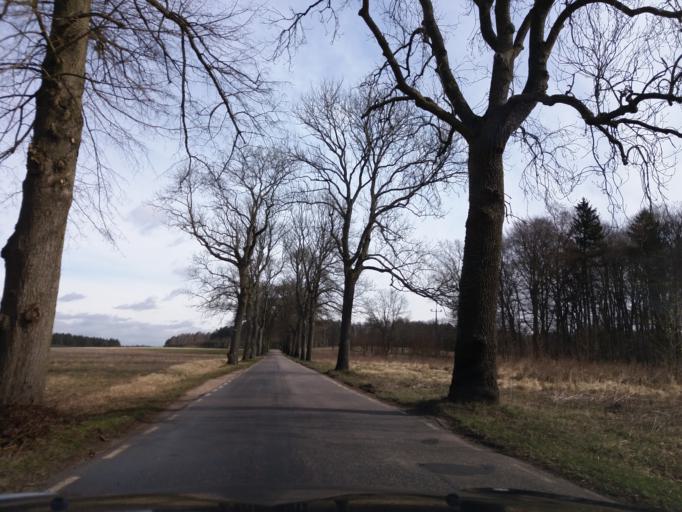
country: PL
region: West Pomeranian Voivodeship
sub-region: Powiat drawski
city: Kalisz Pomorski
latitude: 53.2601
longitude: 15.8583
